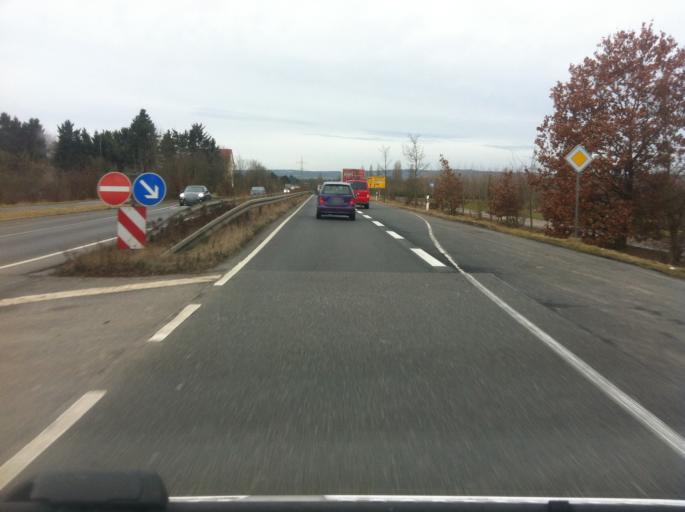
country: DE
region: North Rhine-Westphalia
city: Meckenheim
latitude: 50.6428
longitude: 7.0384
